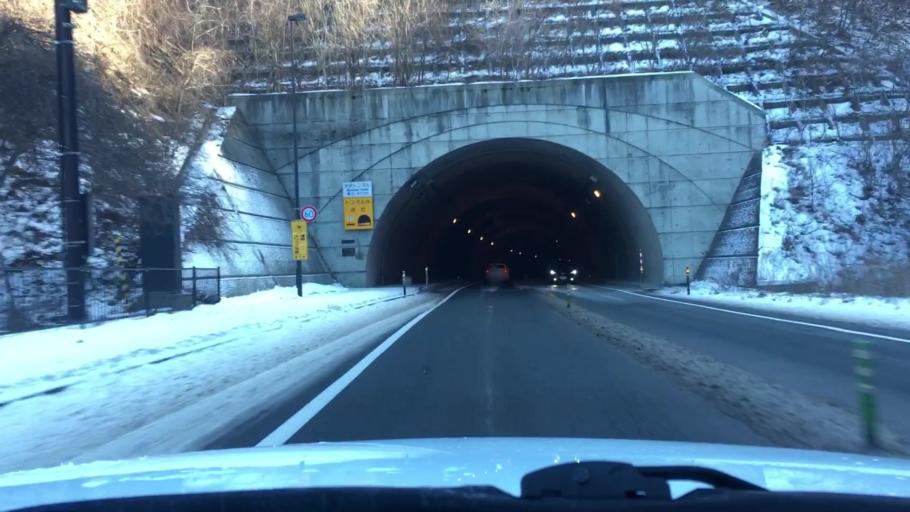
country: JP
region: Iwate
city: Morioka-shi
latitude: 39.6737
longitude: 141.2802
